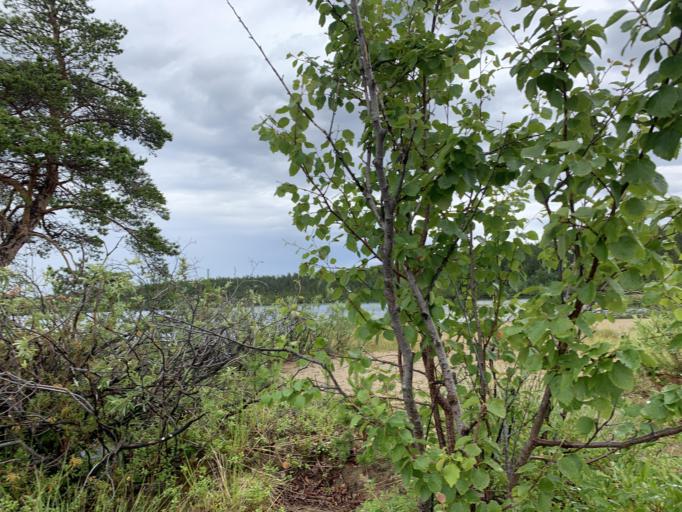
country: RU
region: Murmansk
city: Monchegorsk
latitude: 67.9546
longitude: 33.0259
